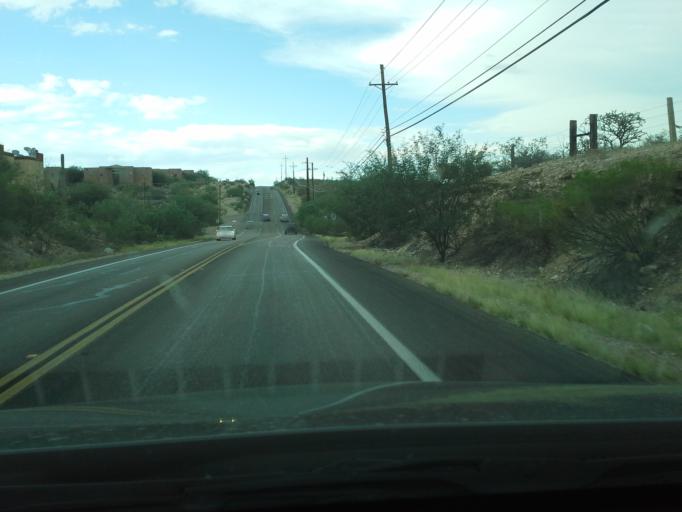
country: US
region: Arizona
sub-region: Pima County
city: South Tucson
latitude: 32.2198
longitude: -111.0203
